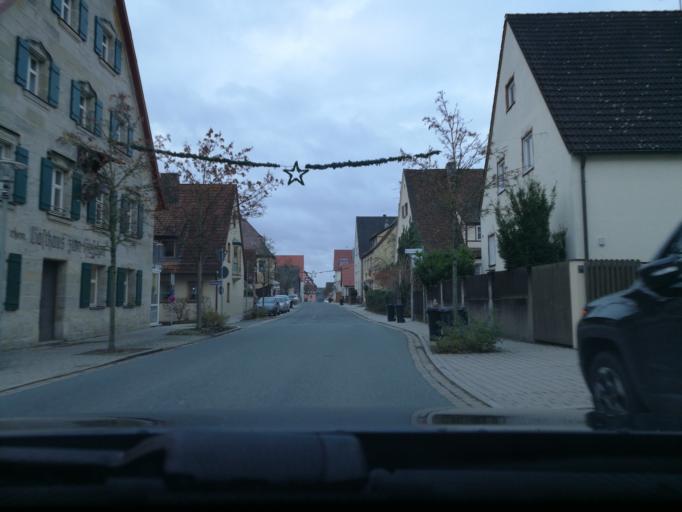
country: DE
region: Bavaria
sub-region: Regierungsbezirk Mittelfranken
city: Heroldsberg
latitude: 49.5366
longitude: 11.1548
